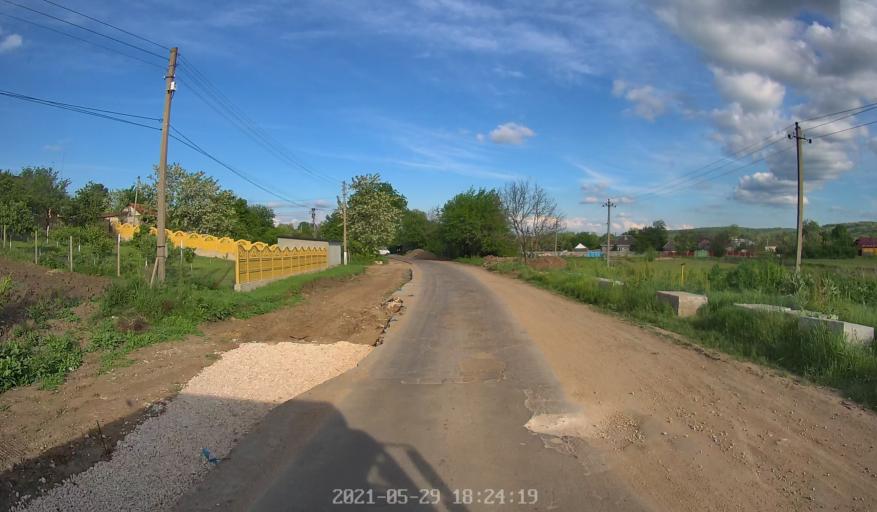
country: MD
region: Chisinau
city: Singera
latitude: 46.8300
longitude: 28.8621
